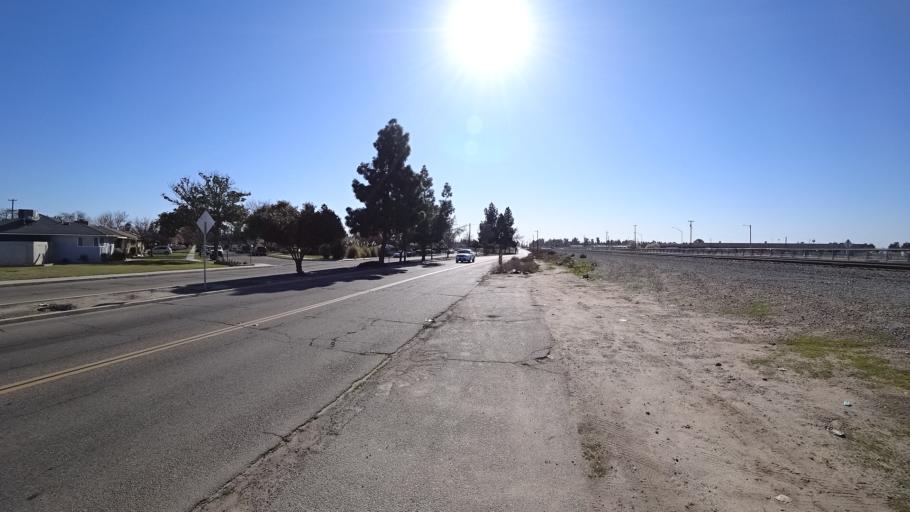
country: US
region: California
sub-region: Fresno County
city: West Park
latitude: 36.7675
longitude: -119.8319
